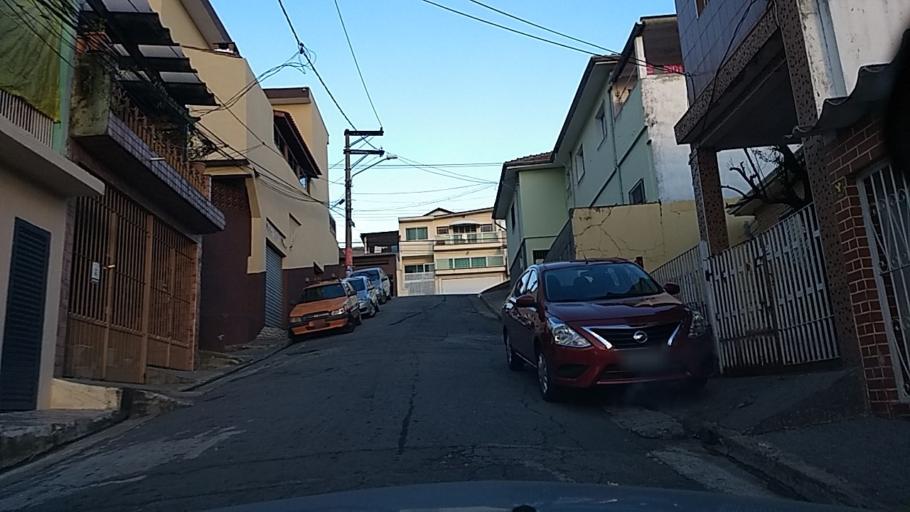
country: BR
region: Sao Paulo
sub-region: Guarulhos
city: Guarulhos
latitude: -23.4859
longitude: -46.5845
